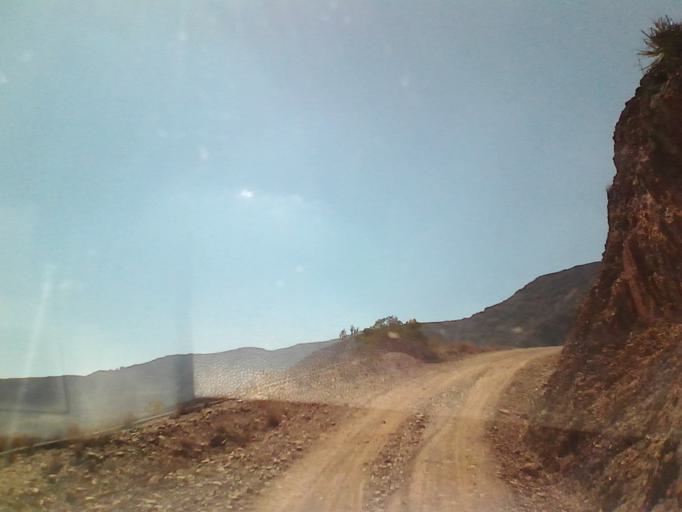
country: CO
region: Boyaca
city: Sachica
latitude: 5.5631
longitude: -73.5587
